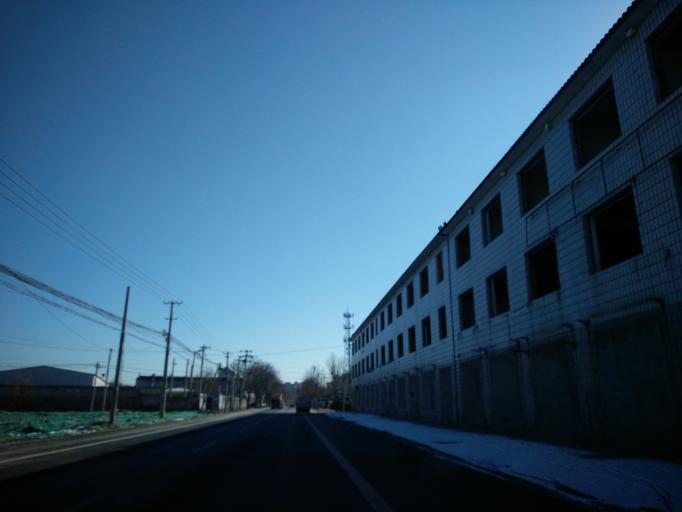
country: CN
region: Beijing
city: Yinghai
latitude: 39.7531
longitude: 116.4656
